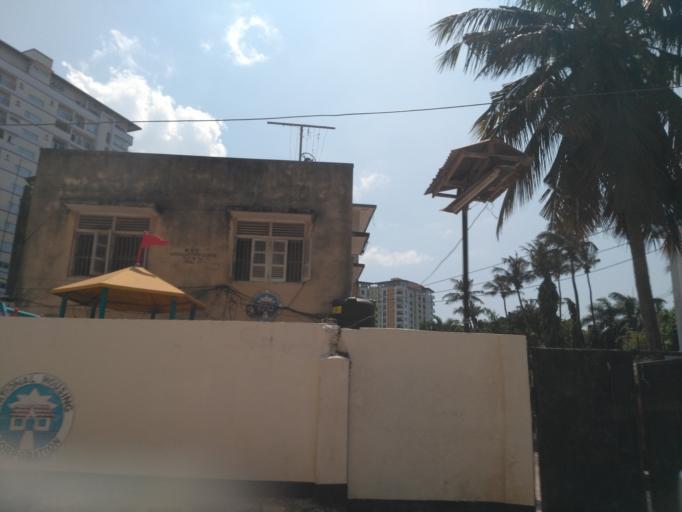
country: TZ
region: Dar es Salaam
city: Dar es Salaam
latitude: -6.8066
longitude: 39.2832
